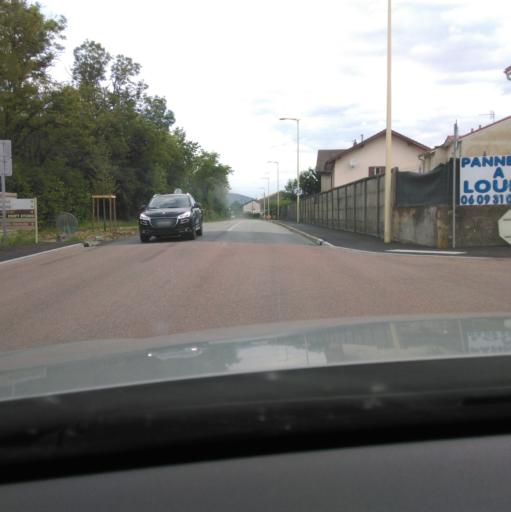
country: FR
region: Rhone-Alpes
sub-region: Departement de l'Ain
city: Izernore
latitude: 46.1891
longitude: 5.5435
